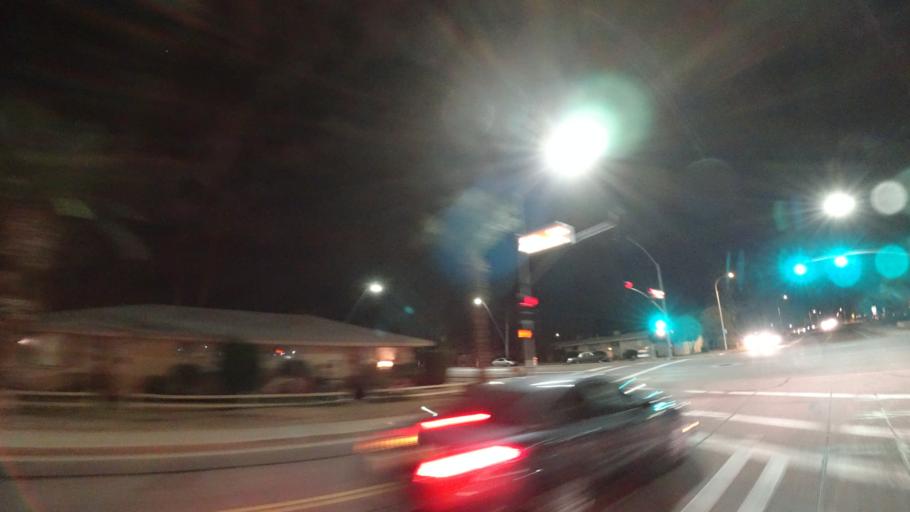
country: US
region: Arizona
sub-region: Maricopa County
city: Chandler
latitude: 33.3097
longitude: -111.8589
